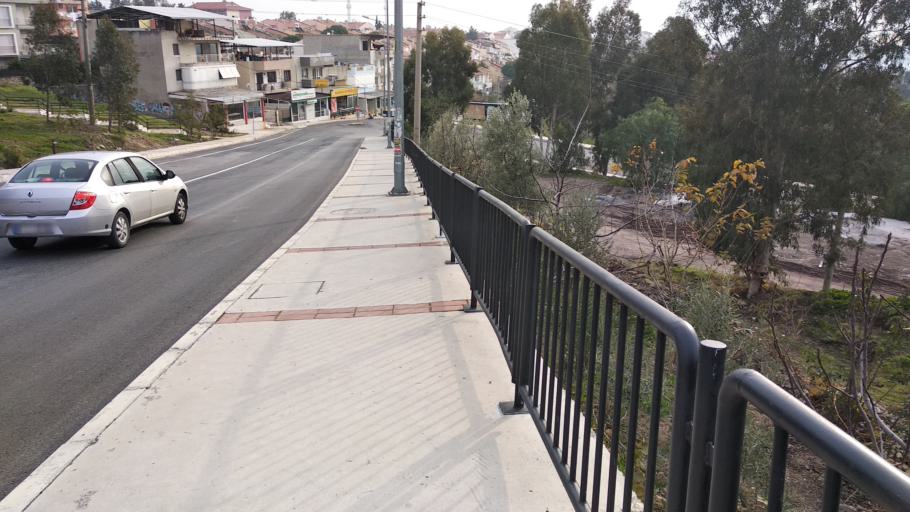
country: TR
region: Izmir
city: Karsiyaka
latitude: 38.4948
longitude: 27.0840
